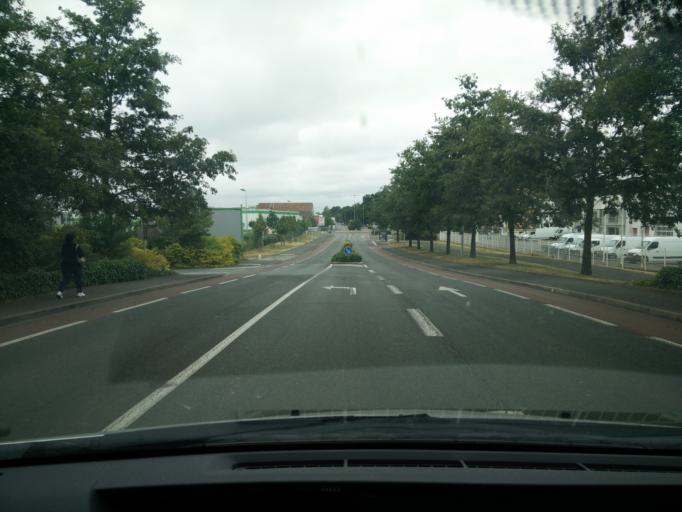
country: FR
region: Pays de la Loire
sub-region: Departement de Maine-et-Loire
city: Angers
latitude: 47.4700
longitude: -0.5134
